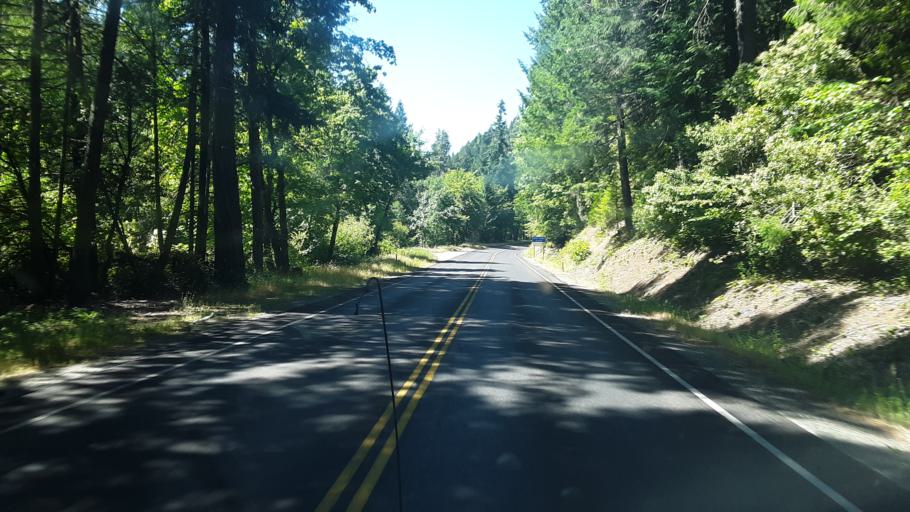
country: US
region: Oregon
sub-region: Josephine County
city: Cave Junction
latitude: 41.9820
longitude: -123.7193
